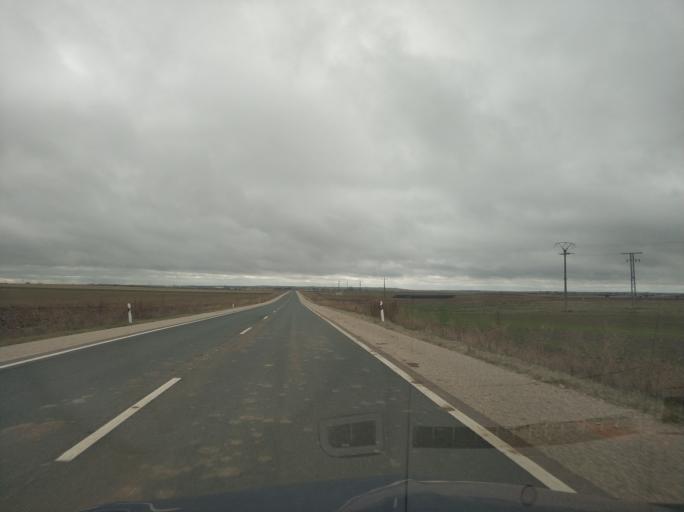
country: ES
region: Castille and Leon
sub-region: Provincia de Salamanca
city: Villaverde de Guarena
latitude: 41.0793
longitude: -5.5229
